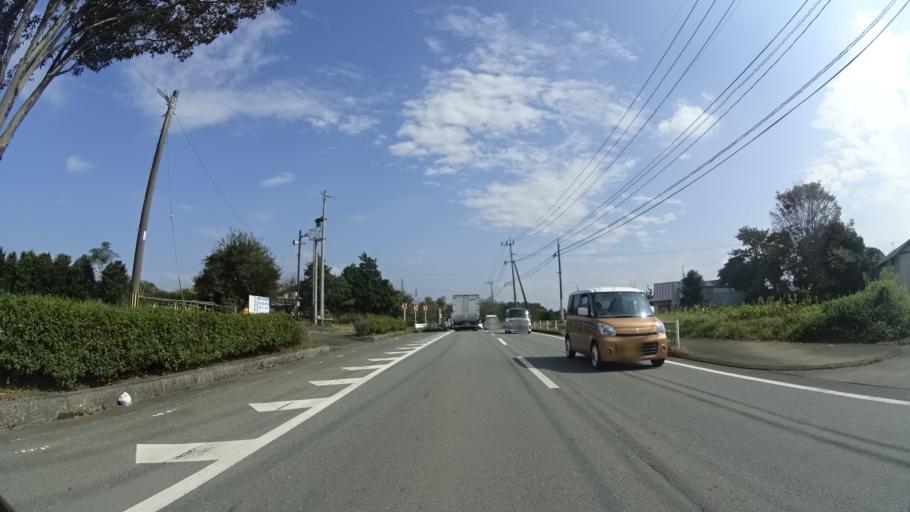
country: JP
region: Kumamoto
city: Kumamoto
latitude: 32.7461
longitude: 130.7748
